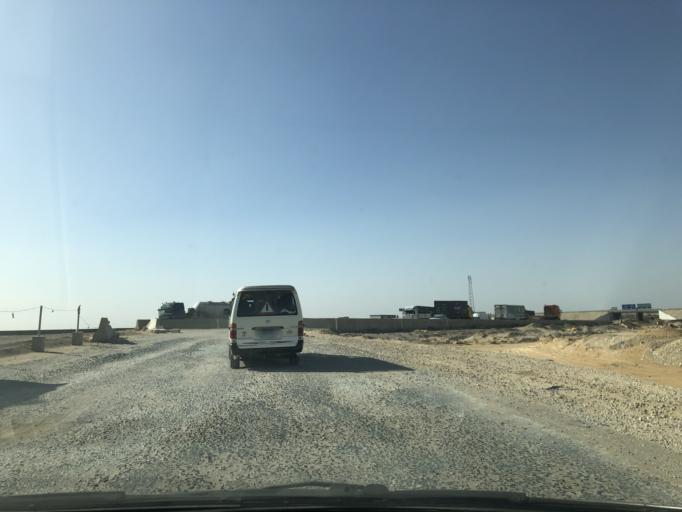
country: EG
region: Muhafazat al Minufiyah
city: Ashmun
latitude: 30.0629
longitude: 30.8462
